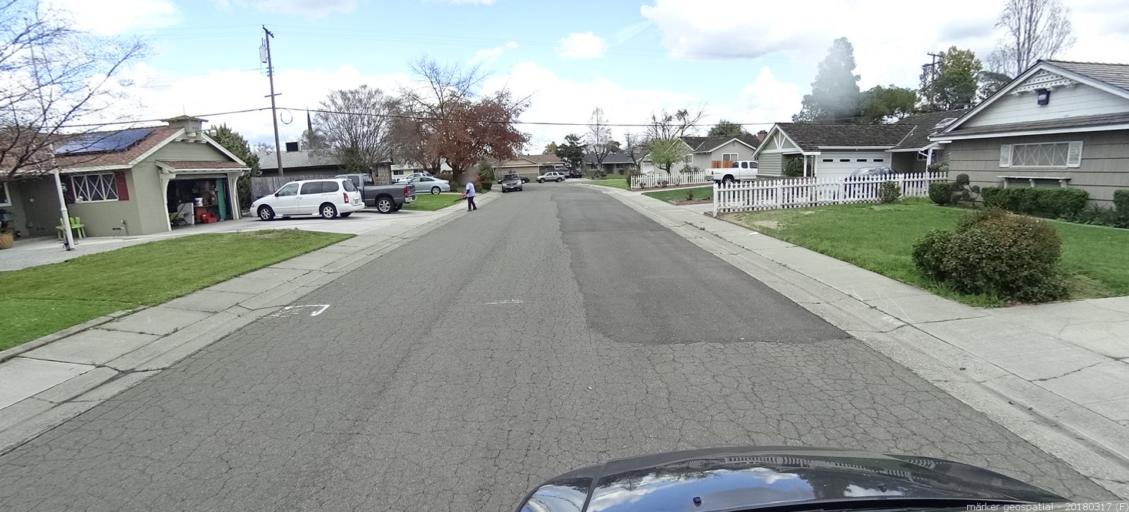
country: US
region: California
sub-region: Sacramento County
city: Parkway
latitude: 38.4992
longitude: -121.4594
